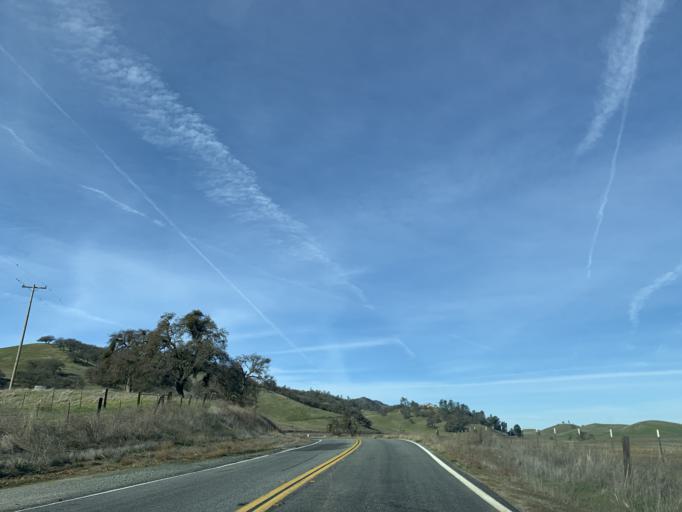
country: US
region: California
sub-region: Monterey County
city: Soledad
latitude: 36.5528
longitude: -121.1663
